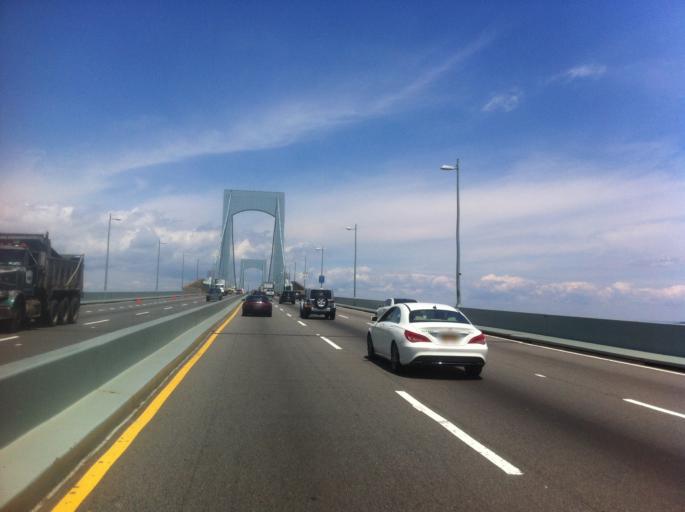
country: US
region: New York
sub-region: Nassau County
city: East Atlantic Beach
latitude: 40.7883
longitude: -73.7907
